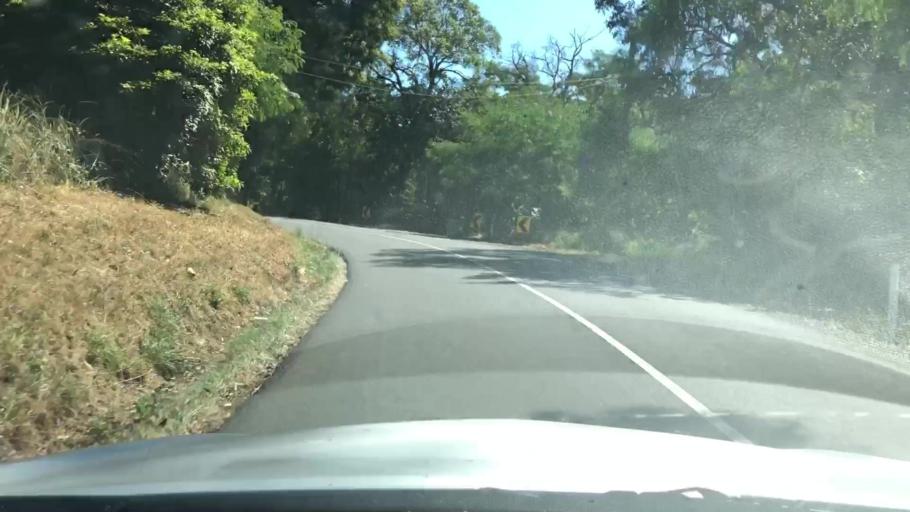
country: AU
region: Victoria
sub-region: Yarra Ranges
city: Macclesfield
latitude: -37.8983
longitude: 145.4703
